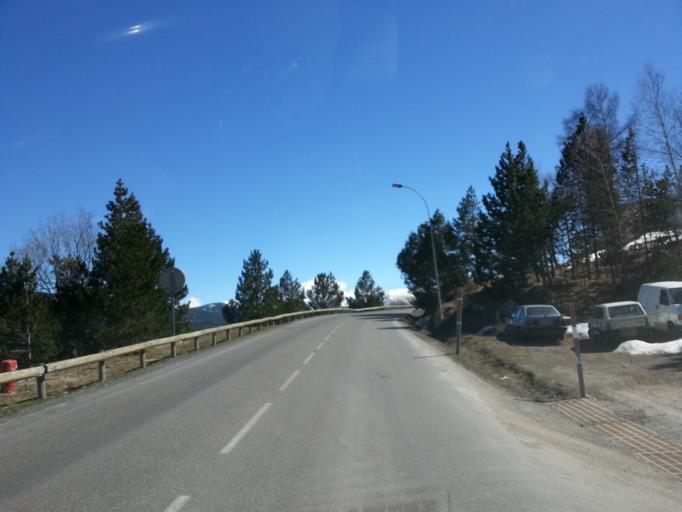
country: ES
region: Catalonia
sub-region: Provincia de Girona
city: Llivia
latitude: 42.5710
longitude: 2.0733
